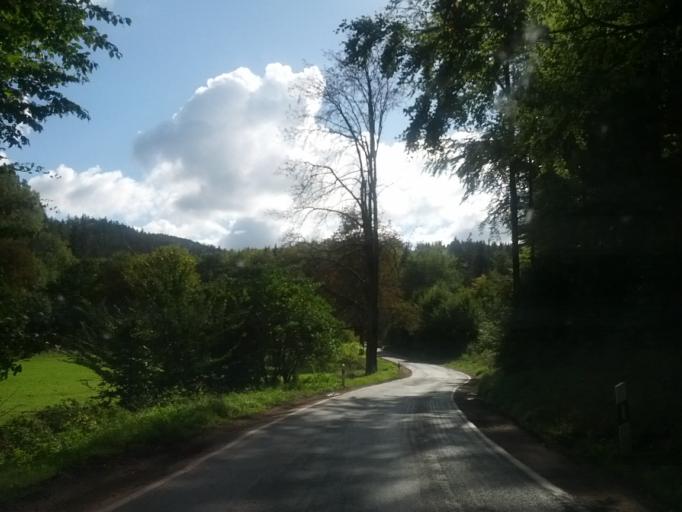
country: DE
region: Thuringia
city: Ruhla
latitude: 50.8990
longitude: 10.3160
